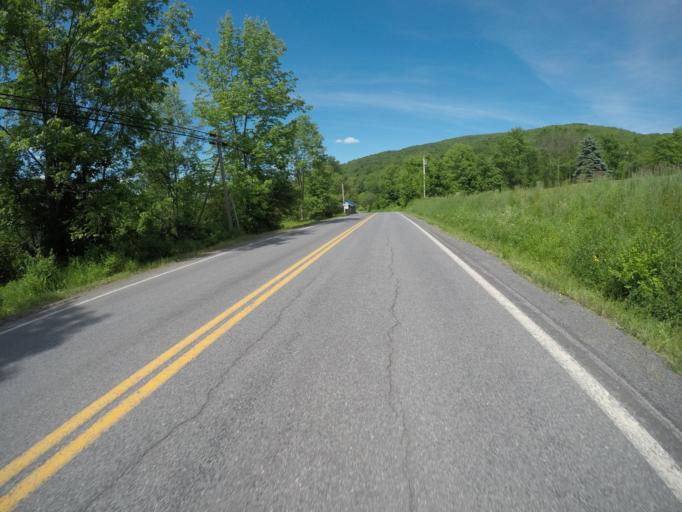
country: US
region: New York
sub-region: Delaware County
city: Delhi
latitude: 42.1419
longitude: -74.7982
